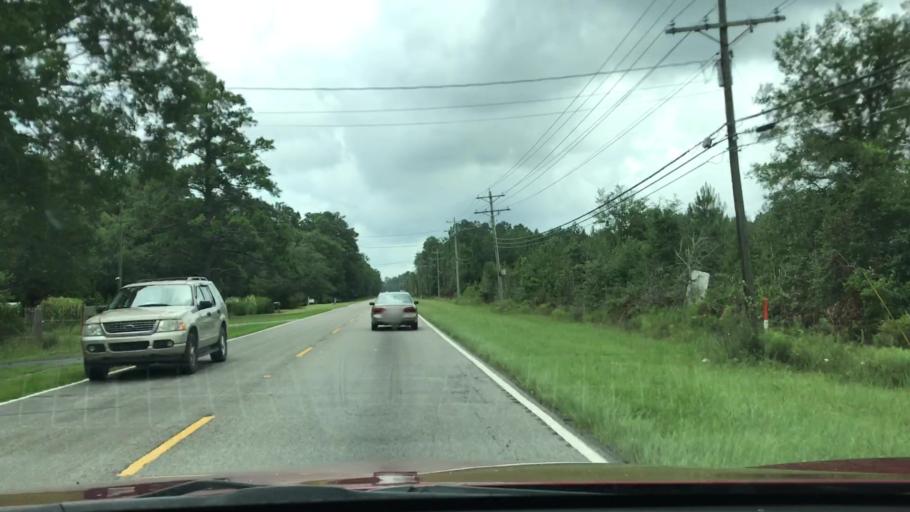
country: US
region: South Carolina
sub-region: Georgetown County
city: Georgetown
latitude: 33.4266
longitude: -79.2803
